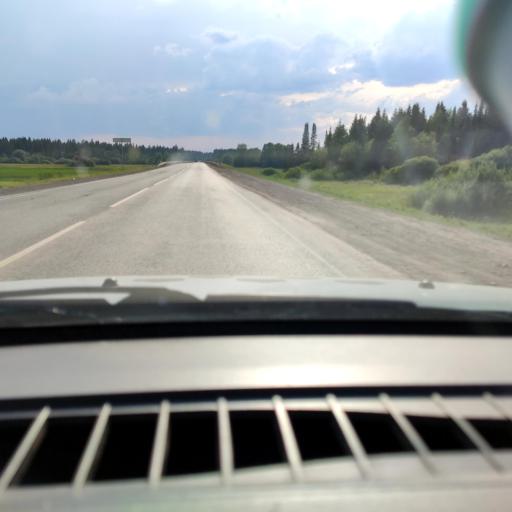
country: RU
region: Udmurtiya
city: Debesy
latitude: 57.6355
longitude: 53.8053
